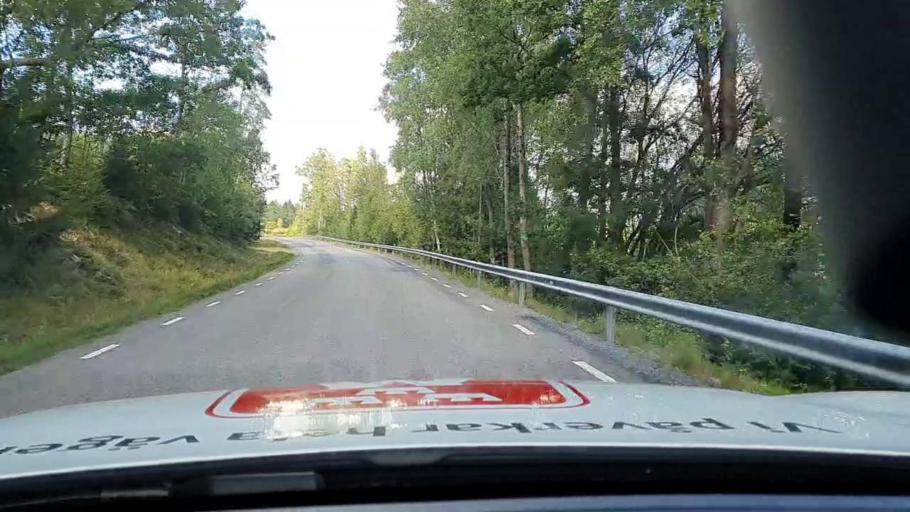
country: SE
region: Vaestra Goetaland
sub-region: Marks Kommun
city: Fritsla
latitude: 57.3664
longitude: 12.8651
